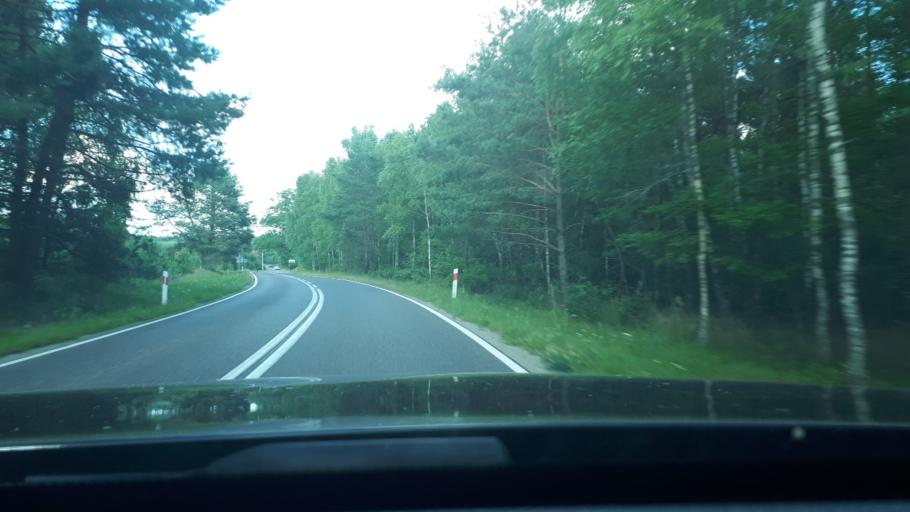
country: PL
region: Warmian-Masurian Voivodeship
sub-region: Powiat olsztynski
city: Stawiguda
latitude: 53.5395
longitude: 20.5415
